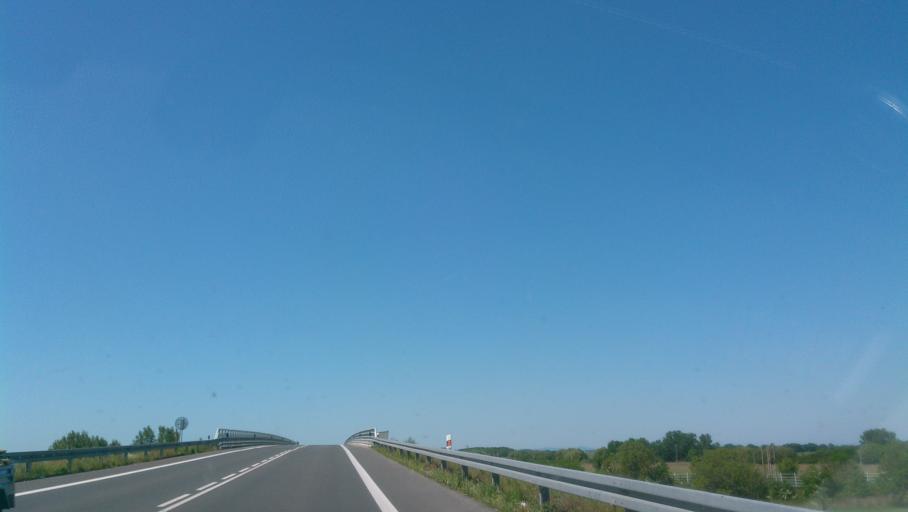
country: SK
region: Trnavsky
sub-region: Okres Galanta
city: Galanta
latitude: 48.1852
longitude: 17.7010
